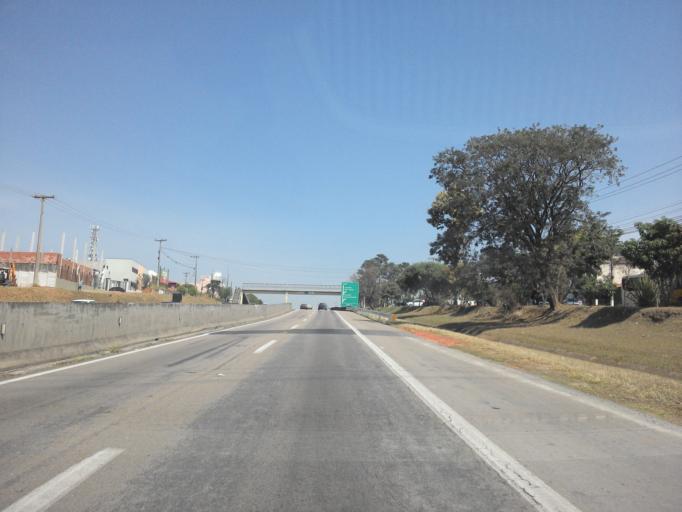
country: BR
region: Sao Paulo
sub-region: Hortolandia
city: Hortolandia
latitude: -22.8989
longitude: -47.1951
